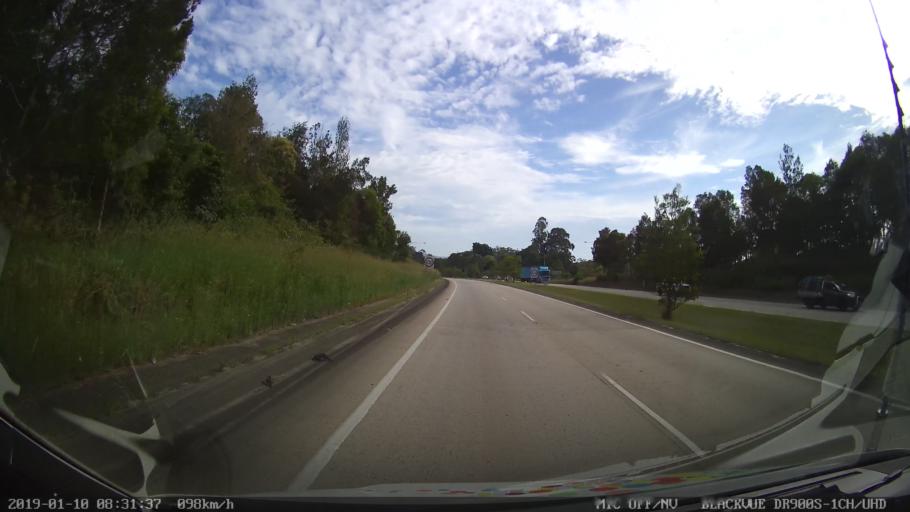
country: AU
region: New South Wales
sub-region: Coffs Harbour
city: Boambee
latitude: -30.3543
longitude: 153.0631
